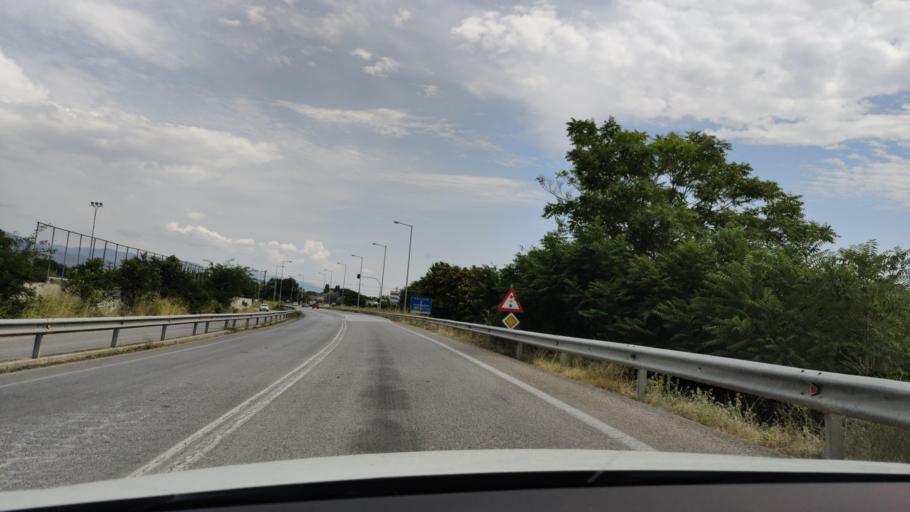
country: GR
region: Central Macedonia
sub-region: Nomos Serron
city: Serres
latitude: 41.0716
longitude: 23.5542
